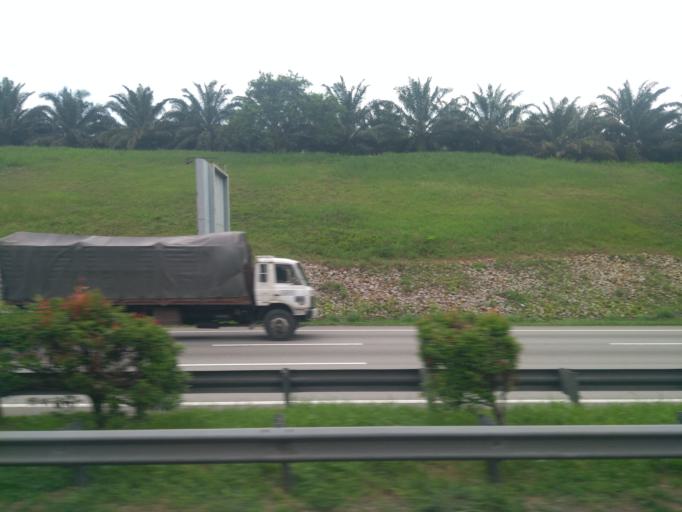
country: MY
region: Melaka
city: Alor Gajah
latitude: 2.3879
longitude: 102.2274
